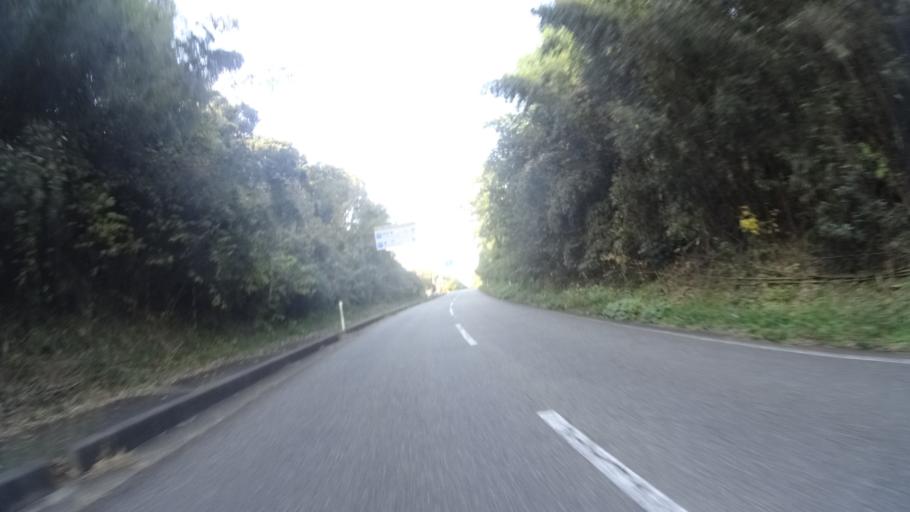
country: JP
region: Ishikawa
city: Hakui
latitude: 37.0895
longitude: 136.7278
